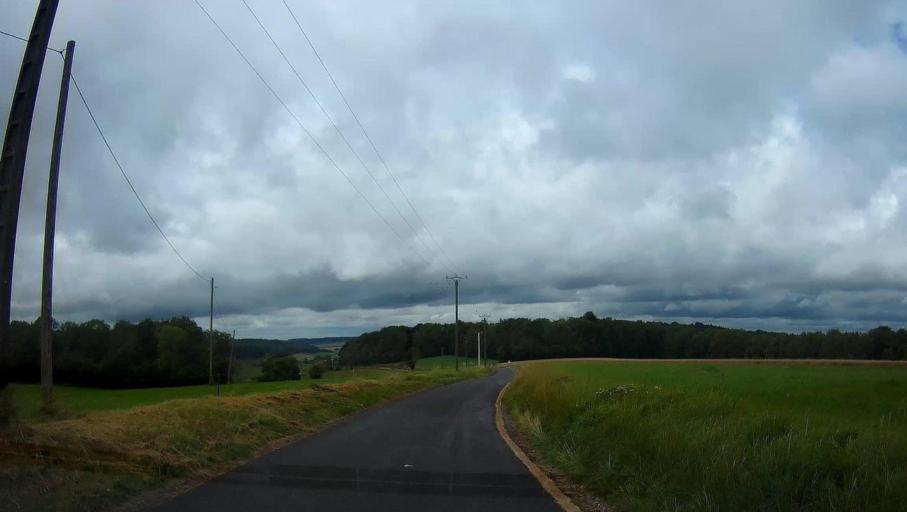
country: FR
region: Champagne-Ardenne
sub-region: Departement des Ardennes
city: Rimogne
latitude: 49.7638
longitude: 4.5035
